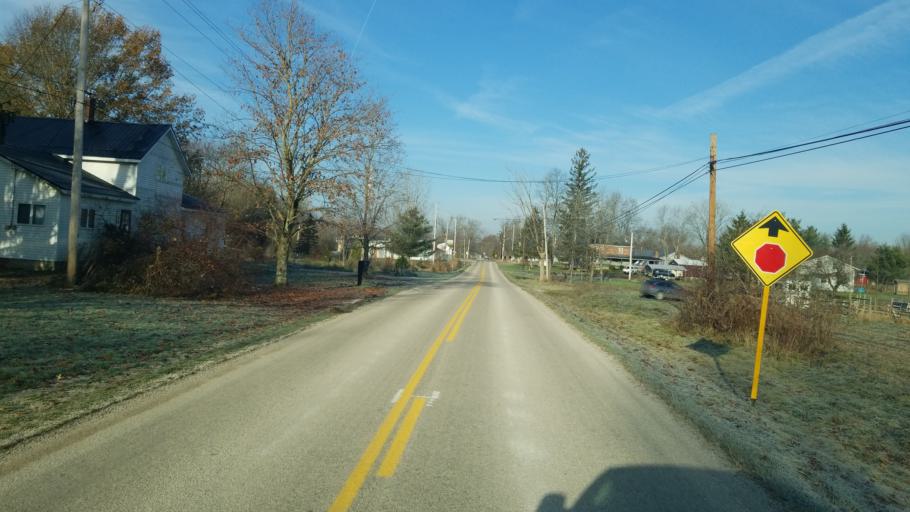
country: US
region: Ohio
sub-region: Ashtabula County
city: Andover
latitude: 41.6752
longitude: -80.6650
